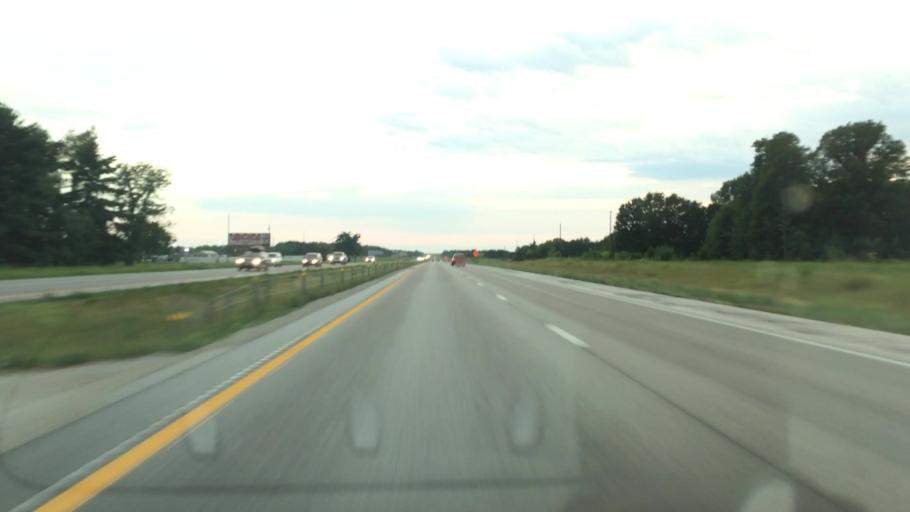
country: US
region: Missouri
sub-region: Greene County
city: Strafford
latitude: 37.2629
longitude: -93.1467
